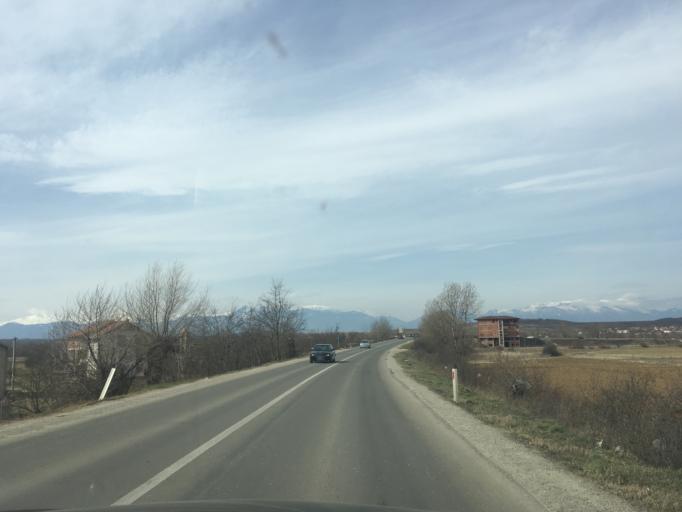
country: XK
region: Pec
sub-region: Komuna e Klines
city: Klina
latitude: 42.5913
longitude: 20.5816
